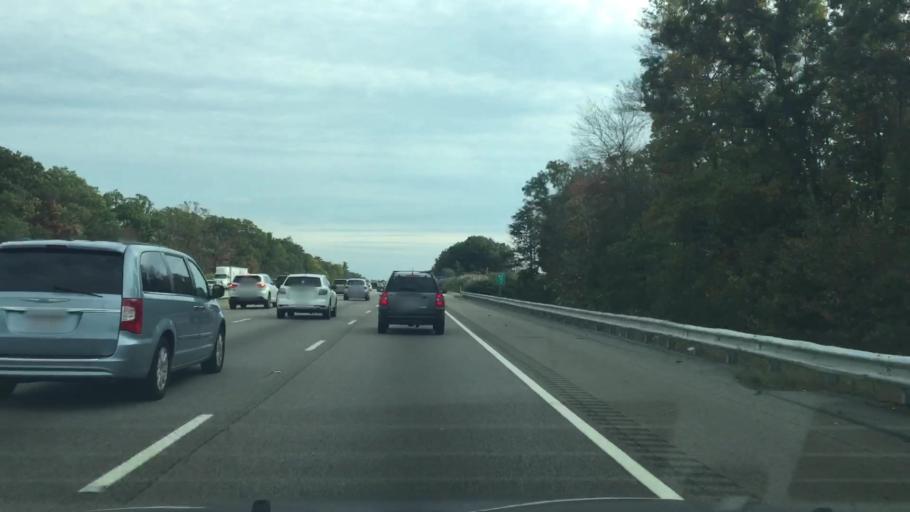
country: US
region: Massachusetts
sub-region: Norfolk County
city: Avon
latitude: 42.1450
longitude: -71.0666
